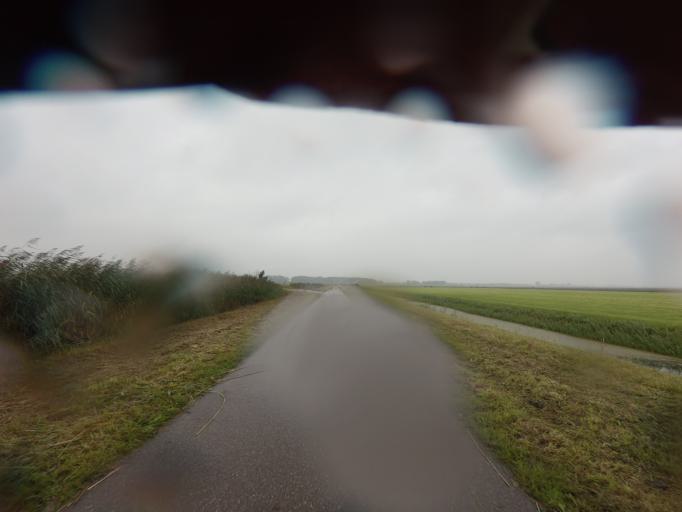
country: NL
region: North Holland
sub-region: Gemeente Medemblik
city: Opperdoes
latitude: 52.7431
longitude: 5.0460
